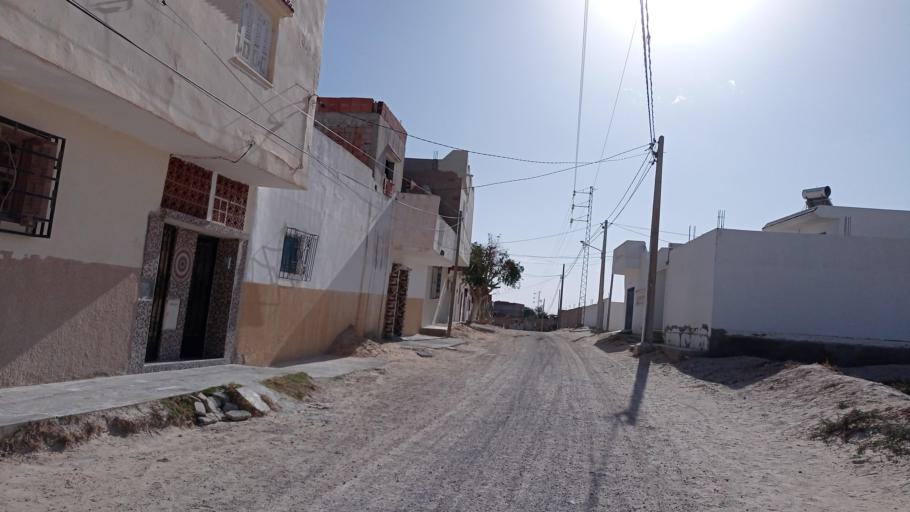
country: TN
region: Qabis
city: Gabes
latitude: 33.8331
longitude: 10.1106
